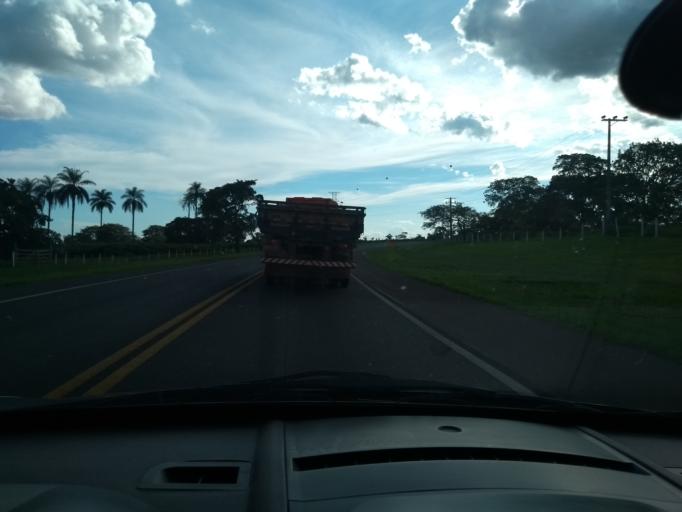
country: BR
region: Sao Paulo
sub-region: Casa Branca
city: Casa Branca
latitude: -21.7973
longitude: -47.0760
